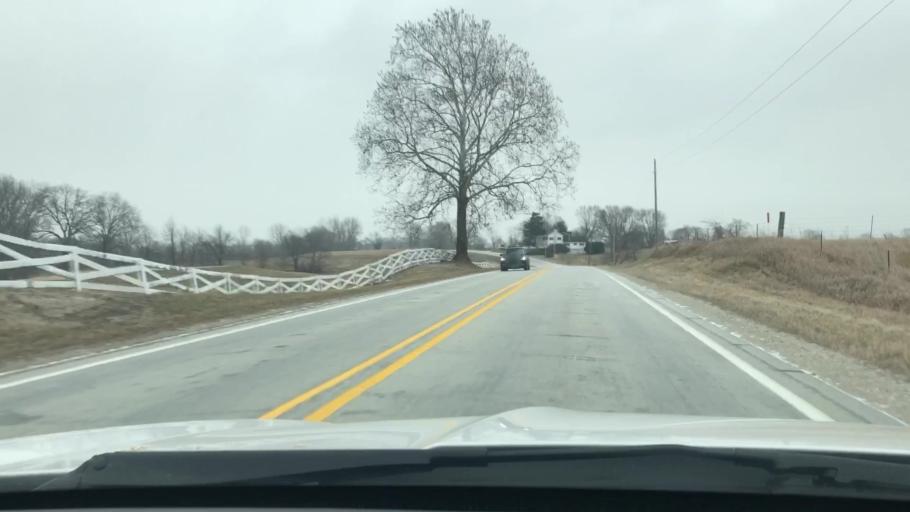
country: US
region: Indiana
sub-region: Fulton County
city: Akron
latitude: 41.0381
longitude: -86.0703
